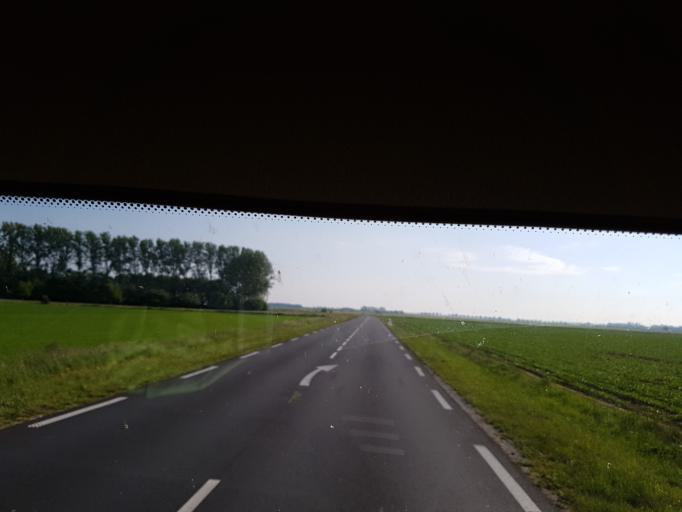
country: FR
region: Picardie
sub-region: Departement de la Somme
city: Crecy-en-Ponthieu
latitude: 50.1926
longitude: 1.8741
